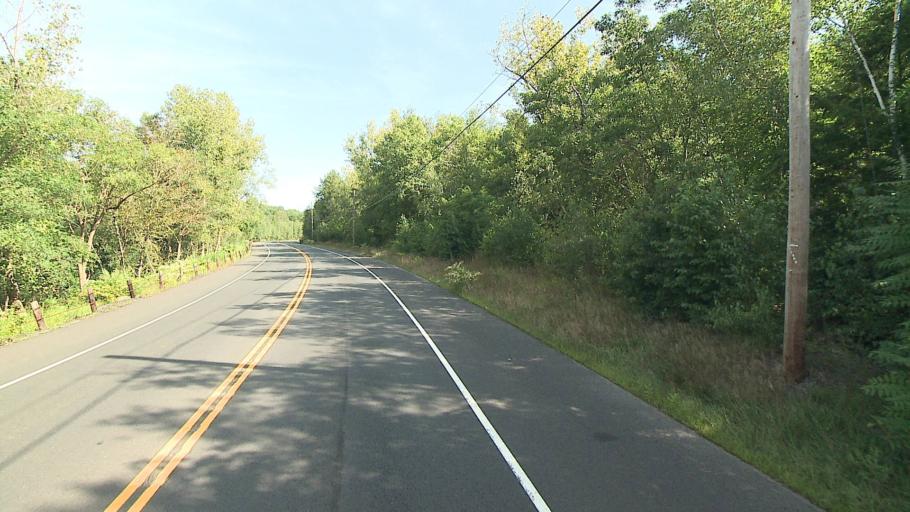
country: US
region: Connecticut
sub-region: Litchfield County
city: Oakville
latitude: 41.6036
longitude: -73.0583
